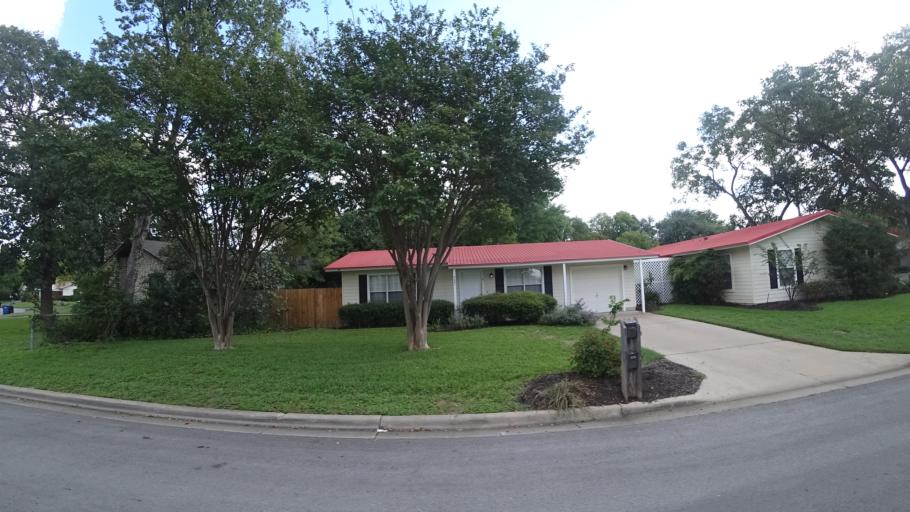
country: US
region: Texas
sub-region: Travis County
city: Austin
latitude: 30.3580
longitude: -97.7293
